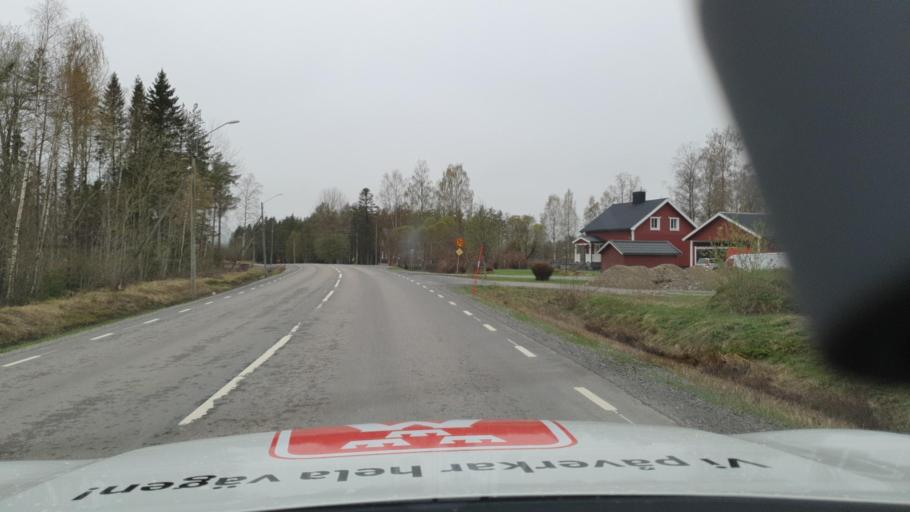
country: SE
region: Vaesterbotten
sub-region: Umea Kommun
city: Hoernefors
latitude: 63.7786
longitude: 19.8791
